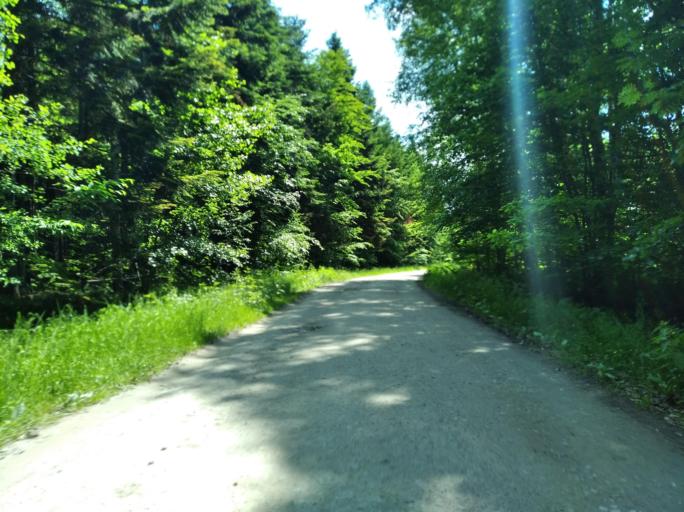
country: PL
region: Subcarpathian Voivodeship
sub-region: Powiat ropczycko-sedziszowski
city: Zagorzyce
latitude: 49.9734
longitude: 21.6849
